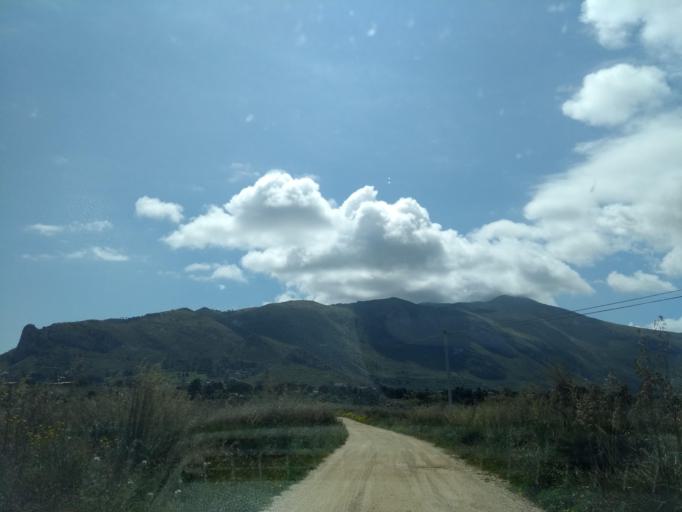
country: IT
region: Sicily
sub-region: Trapani
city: Castellammare del Golfo
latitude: 38.0466
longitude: 12.8483
